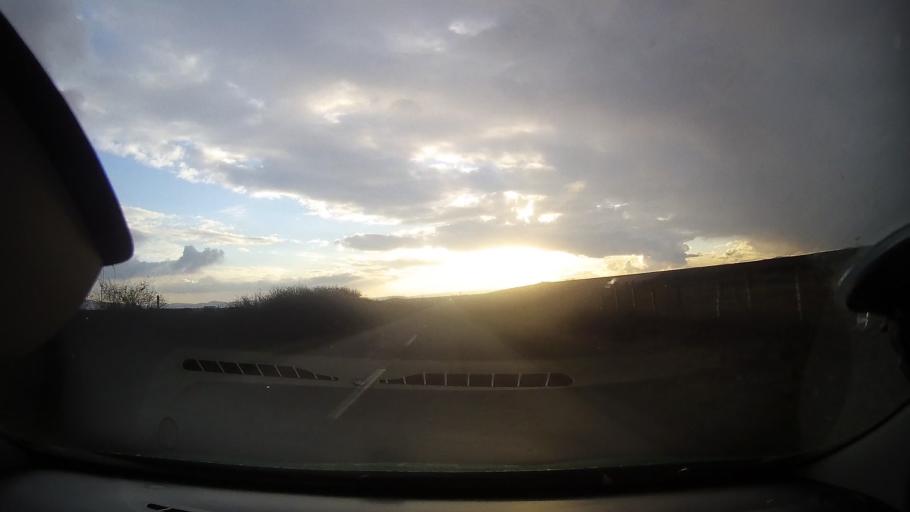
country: RO
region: Alba
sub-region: Comuna Lunca Muresului
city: Lunca Muresului
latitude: 46.4463
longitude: 23.9158
